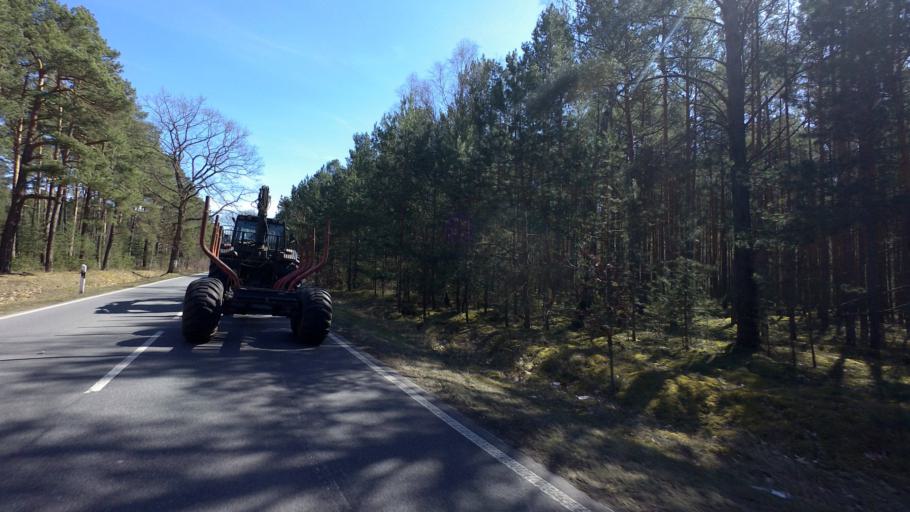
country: DE
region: Brandenburg
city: Halbe
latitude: 52.1139
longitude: 13.6620
